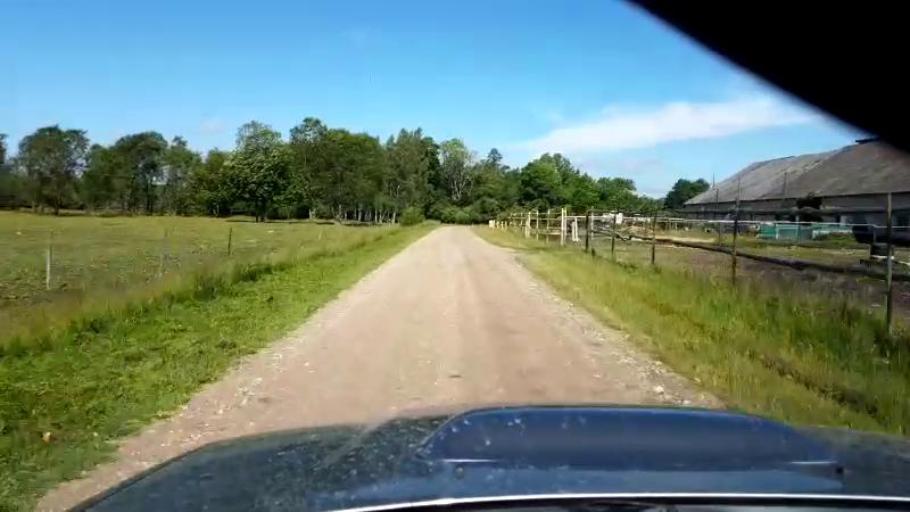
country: EE
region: Paernumaa
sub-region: Sindi linn
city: Sindi
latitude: 58.5154
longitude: 24.6644
